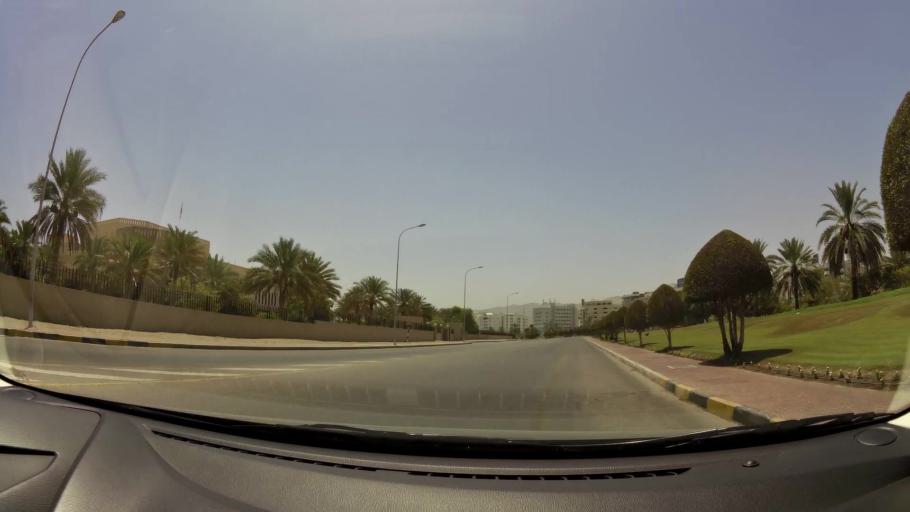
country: OM
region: Muhafazat Masqat
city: Bawshar
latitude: 23.5984
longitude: 58.4248
